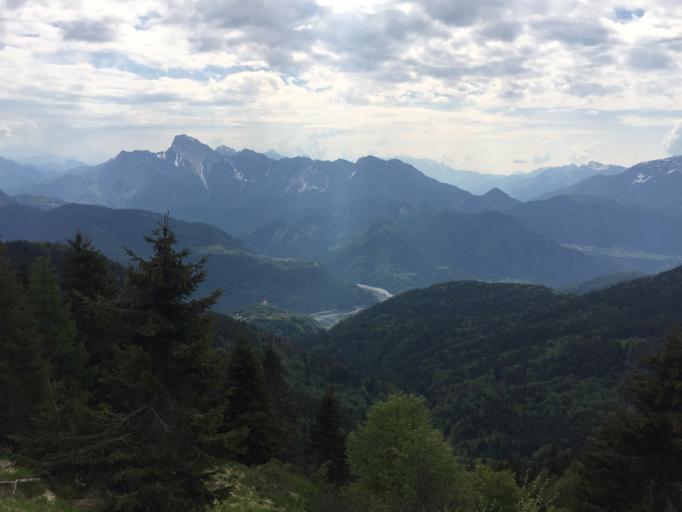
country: IT
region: Friuli Venezia Giulia
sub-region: Provincia di Udine
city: Sutrio
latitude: 46.4711
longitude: 12.9722
